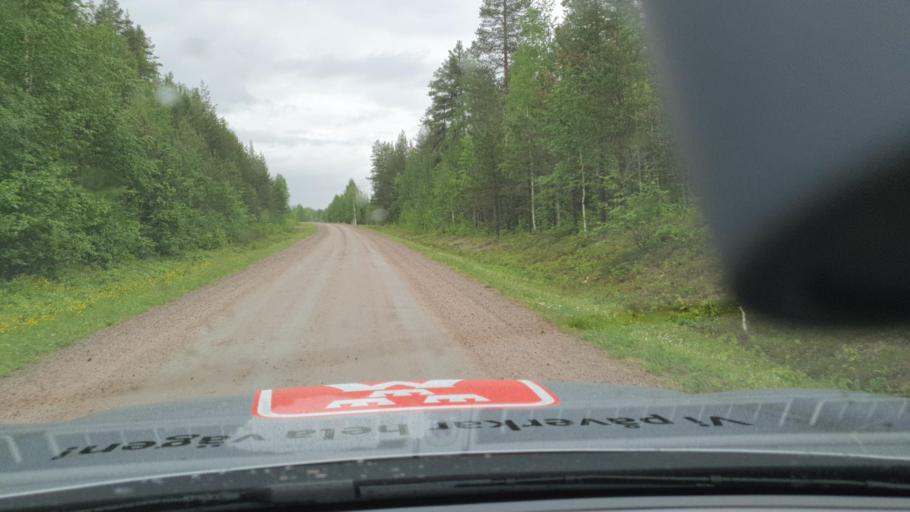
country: SE
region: Norrbotten
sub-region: Overkalix Kommun
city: OEverkalix
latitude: 66.5931
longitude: 22.7478
